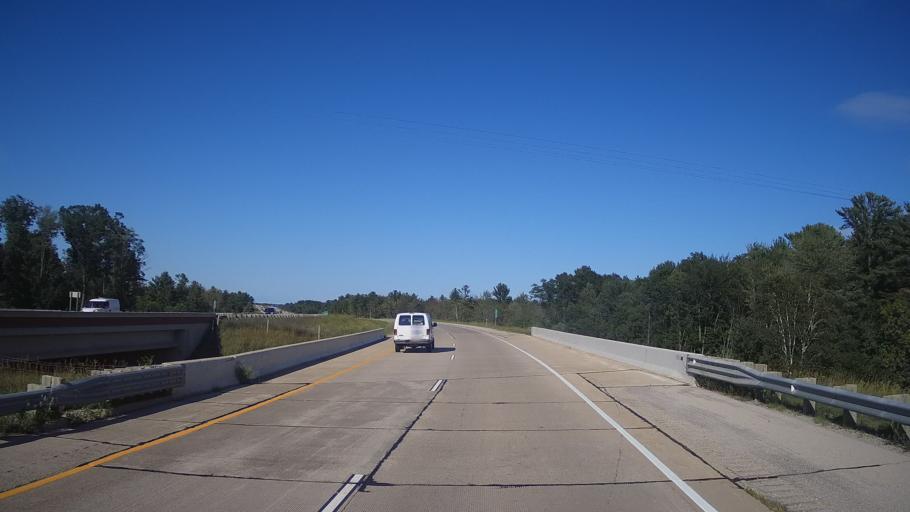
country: US
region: Wisconsin
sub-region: Marinette County
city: Peshtigo
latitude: 45.0408
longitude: -87.7353
